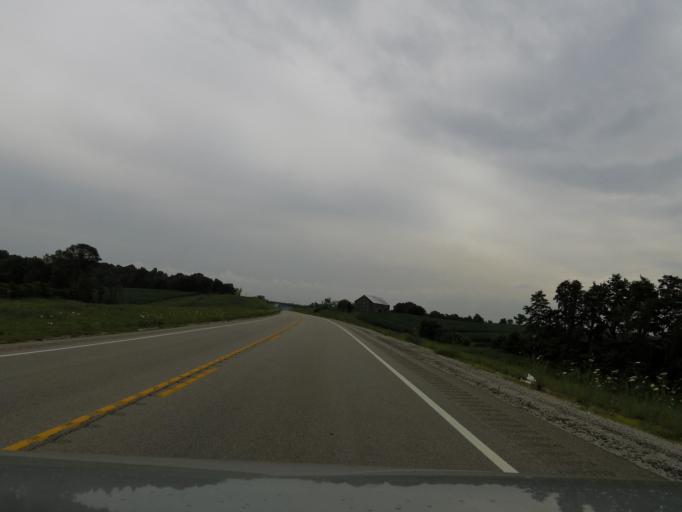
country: US
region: Ohio
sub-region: Brown County
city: Aberdeen
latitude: 38.6147
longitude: -83.8372
